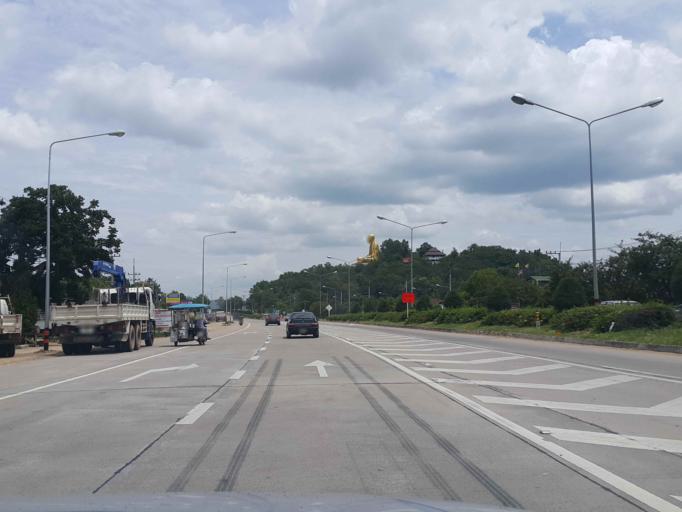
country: TH
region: Lamphun
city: Lamphun
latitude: 18.5514
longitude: 99.0499
